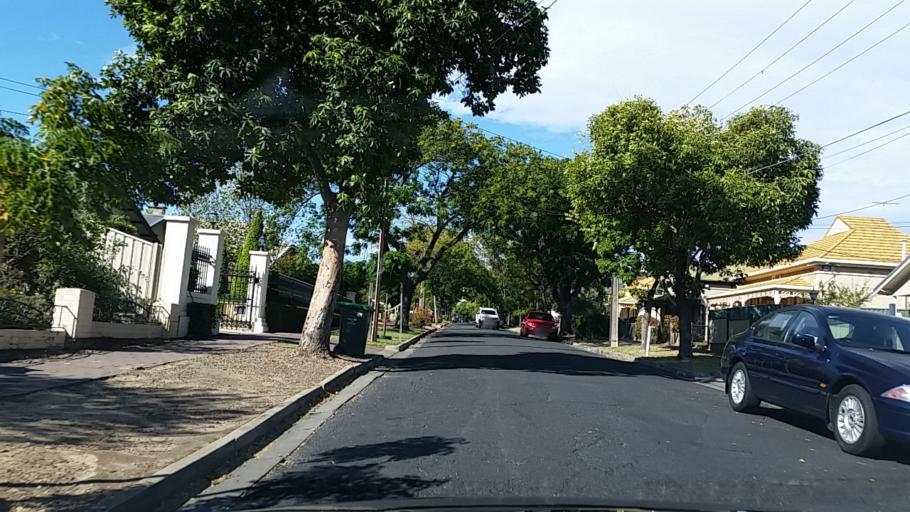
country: AU
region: South Australia
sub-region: Prospect
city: Prospect
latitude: -34.8851
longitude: 138.5945
